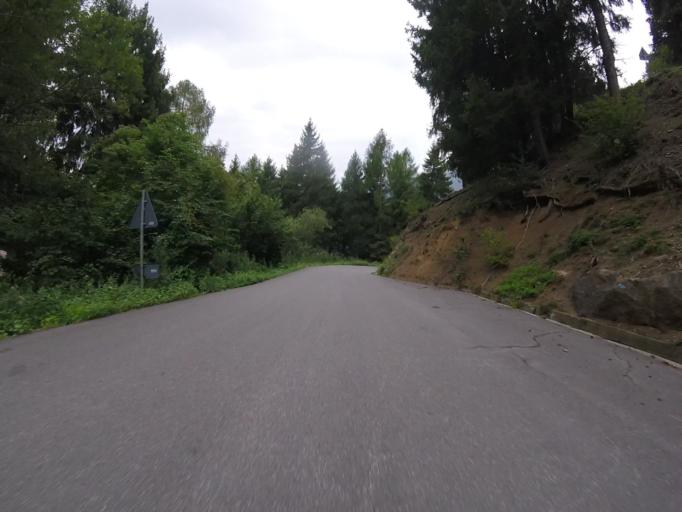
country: IT
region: Lombardy
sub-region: Provincia di Brescia
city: Monno
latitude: 46.2169
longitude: 10.3426
